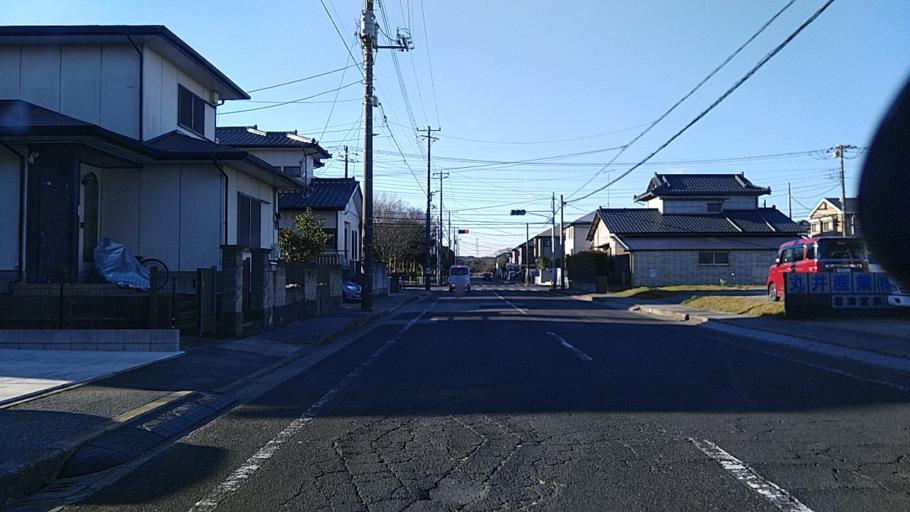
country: JP
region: Chiba
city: Kimitsu
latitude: 35.3312
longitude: 139.8882
